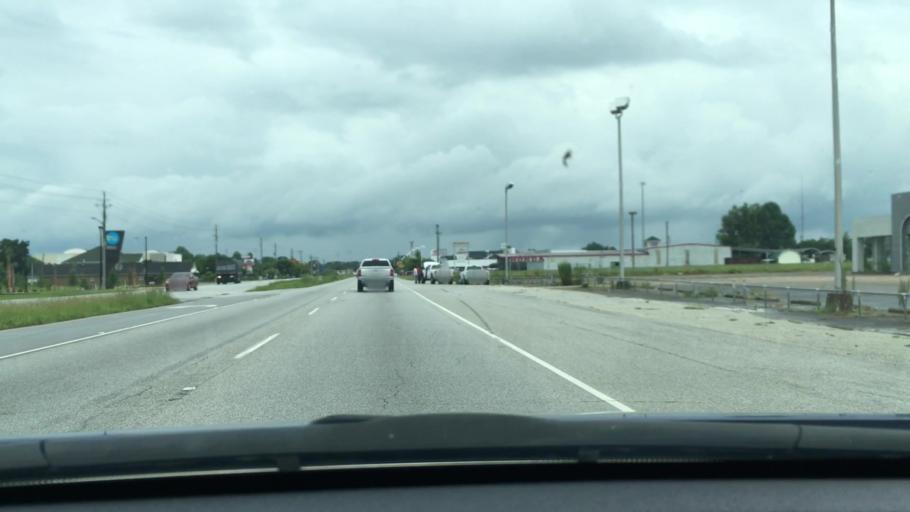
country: US
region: South Carolina
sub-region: Sumter County
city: Cherryvale
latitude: 33.9615
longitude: -80.4004
